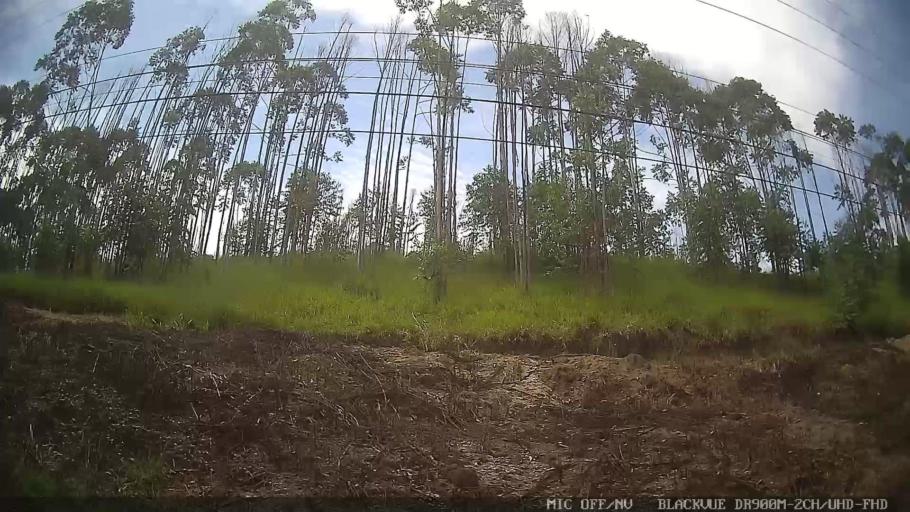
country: BR
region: Sao Paulo
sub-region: Santa Isabel
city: Santa Isabel
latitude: -23.3988
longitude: -46.1953
